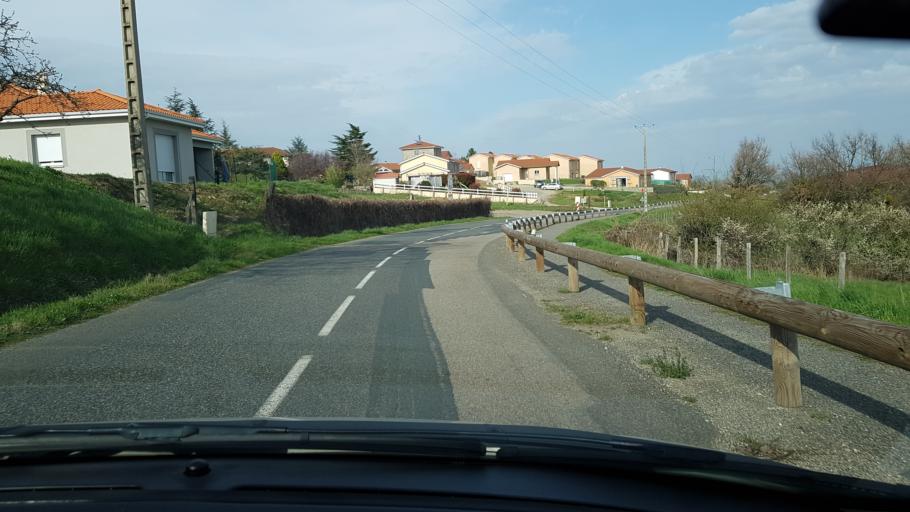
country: FR
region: Rhone-Alpes
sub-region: Departement du Rhone
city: Saint-Maurice-sur-Dargoire
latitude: 45.5843
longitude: 4.6366
